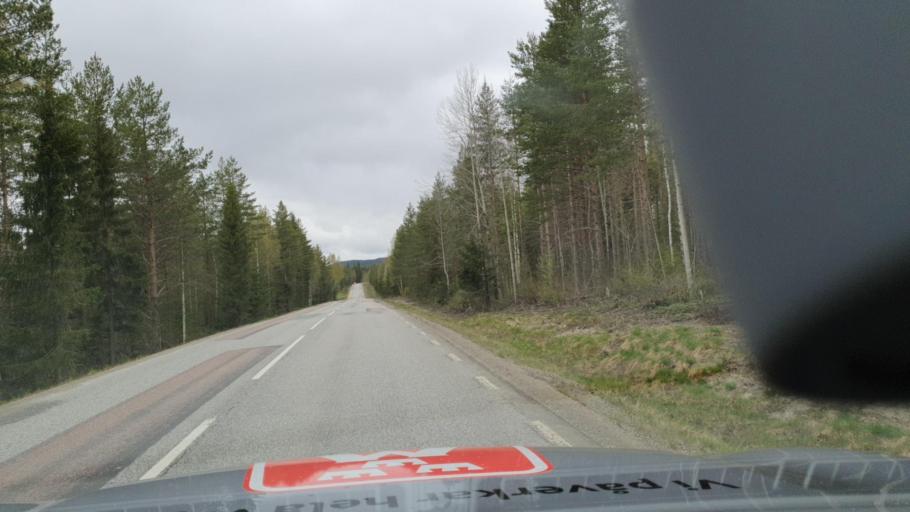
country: SE
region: Vaesternorrland
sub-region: OErnskoeldsviks Kommun
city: Bredbyn
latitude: 63.5496
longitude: 17.6907
